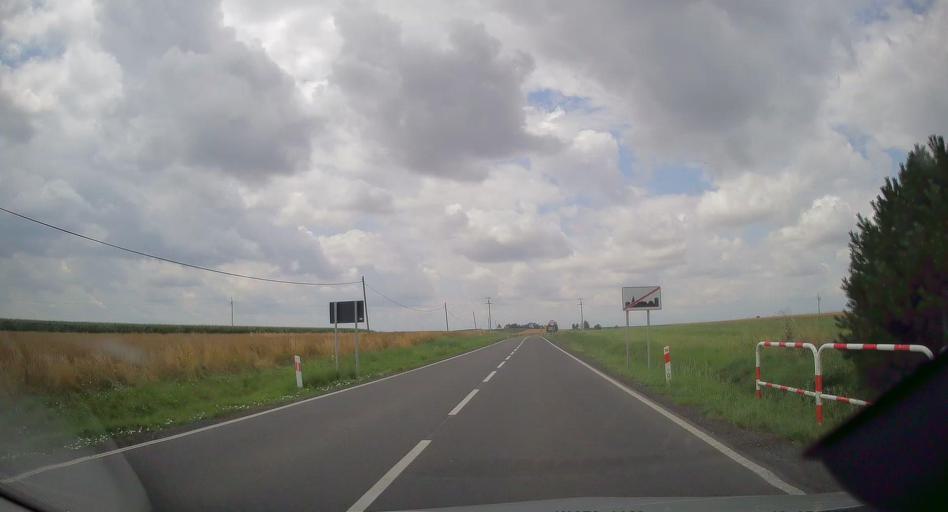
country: PL
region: Opole Voivodeship
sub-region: Powiat prudnicki
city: Glogowek
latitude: 50.3527
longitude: 17.8422
